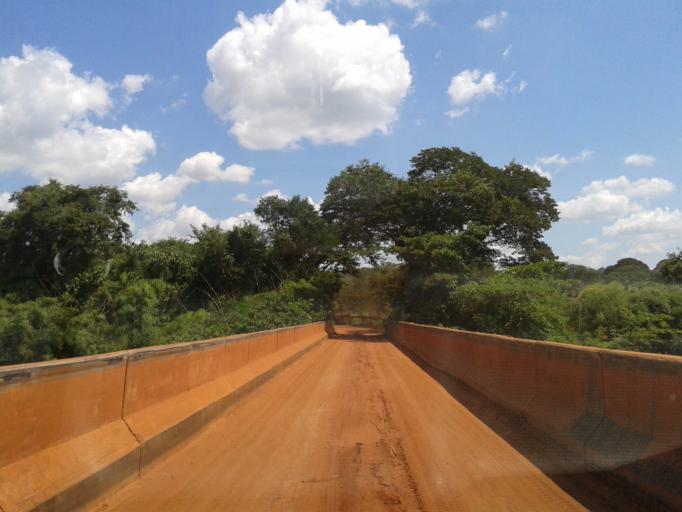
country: BR
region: Minas Gerais
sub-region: Ituiutaba
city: Ituiutaba
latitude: -19.0358
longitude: -49.6974
